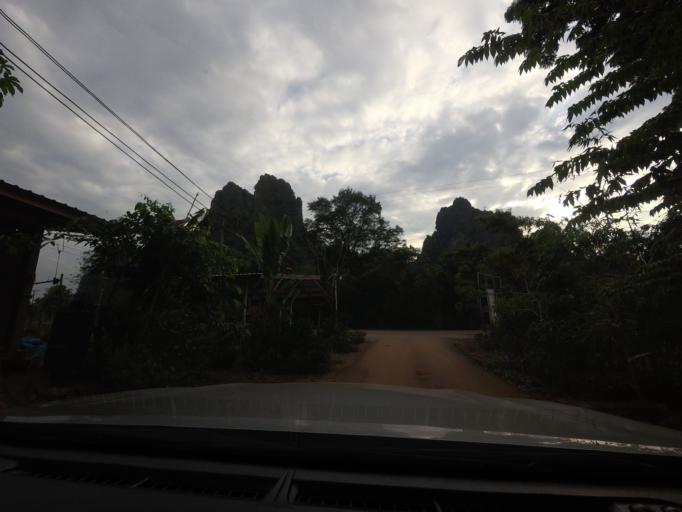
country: TH
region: Phitsanulok
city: Noen Maprang
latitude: 16.5774
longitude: 100.6827
